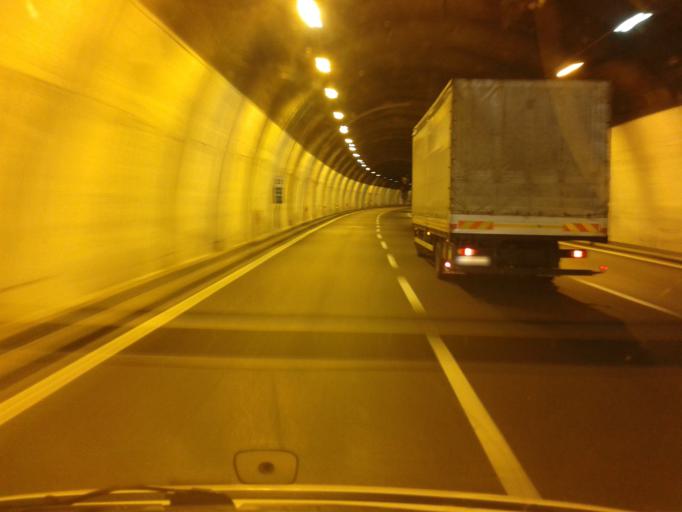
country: IT
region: Liguria
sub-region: Provincia di Genova
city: Rossiglione
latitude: 44.5627
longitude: 8.6652
